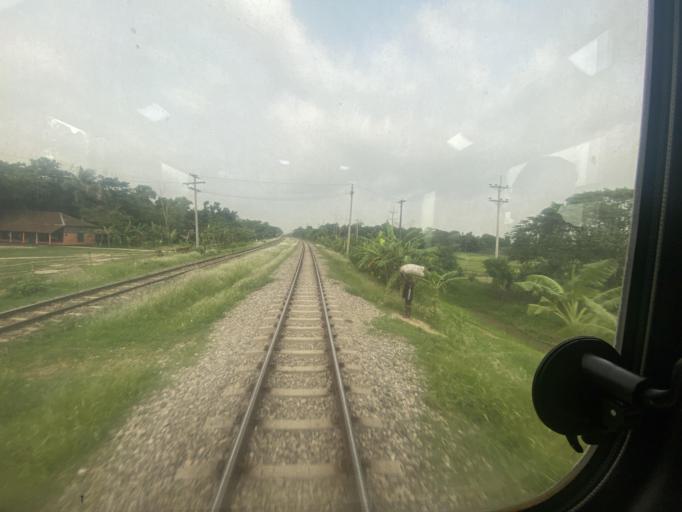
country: BD
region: Dhaka
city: Tungi
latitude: 23.9321
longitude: 90.5244
